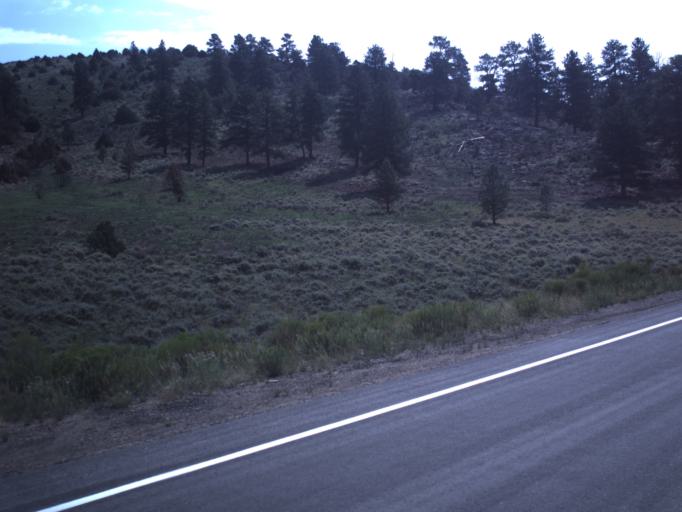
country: US
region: Utah
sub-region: Daggett County
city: Manila
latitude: 40.8867
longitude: -109.7032
